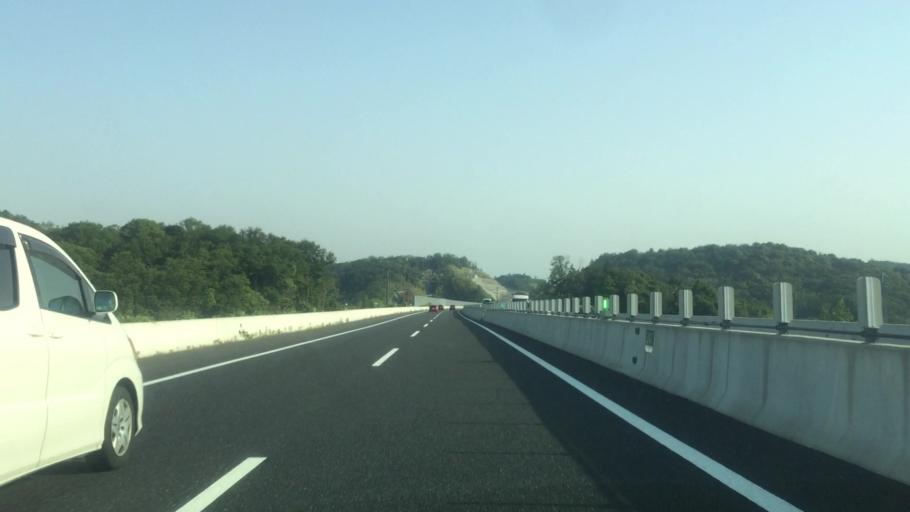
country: JP
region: Aichi
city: Okazaki
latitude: 35.0046
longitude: 137.2298
